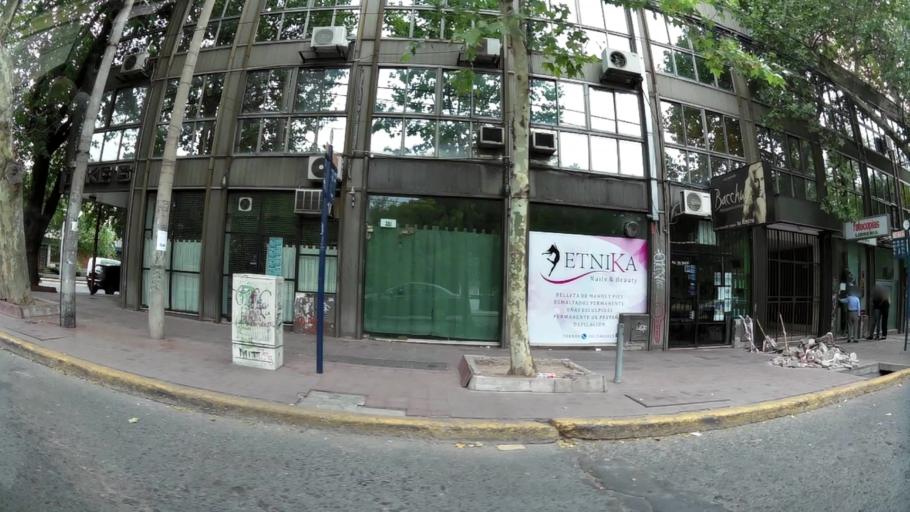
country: AR
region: Mendoza
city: Mendoza
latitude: -32.8962
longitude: -68.8460
